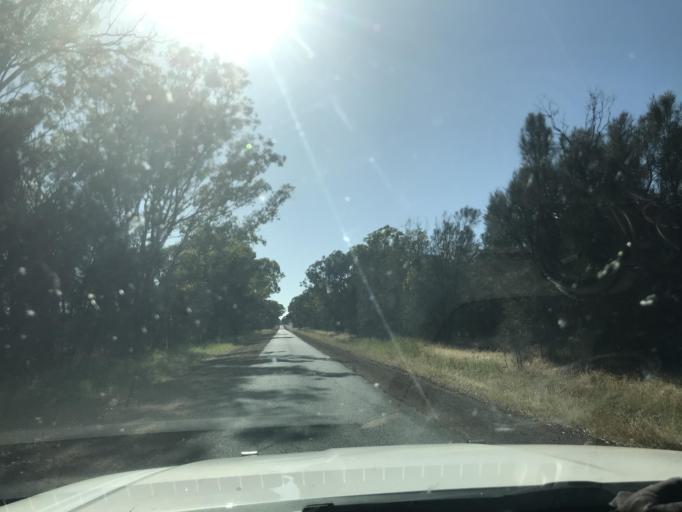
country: AU
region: Victoria
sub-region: Horsham
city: Horsham
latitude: -37.0058
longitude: 141.6287
